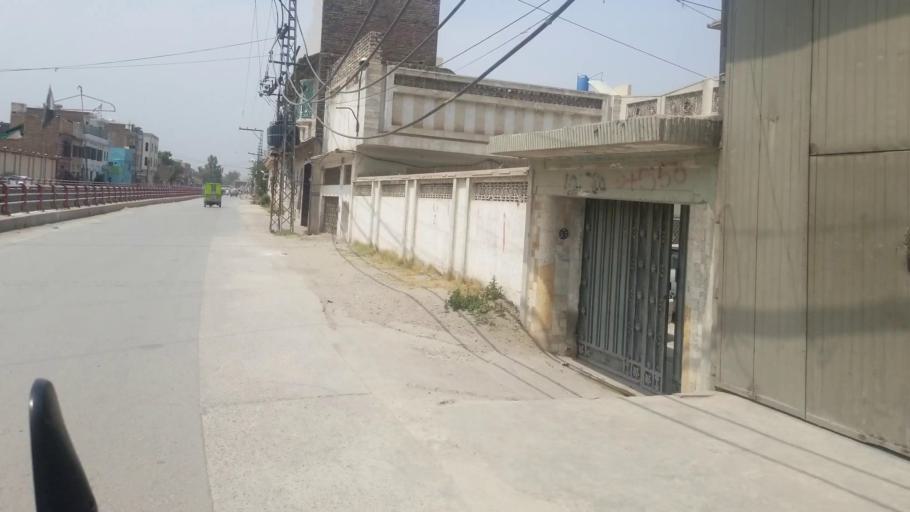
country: PK
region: Khyber Pakhtunkhwa
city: Peshawar
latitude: 34.0134
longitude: 71.6104
